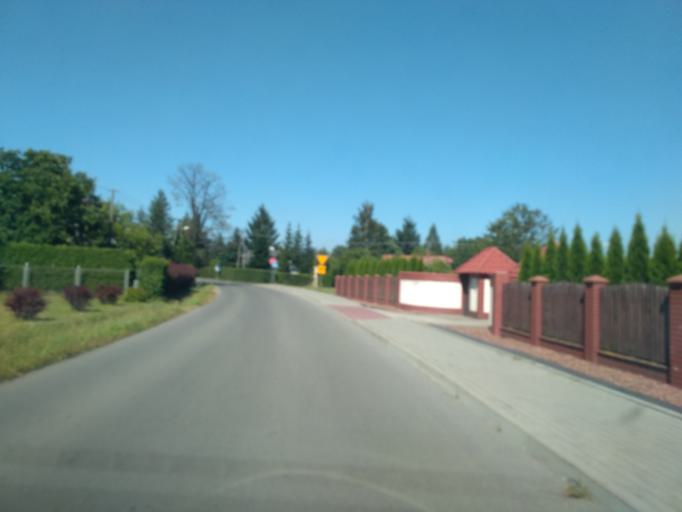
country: PL
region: Subcarpathian Voivodeship
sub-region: Powiat krosnienski
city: Miejsce Piastowe
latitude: 49.6340
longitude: 21.7447
